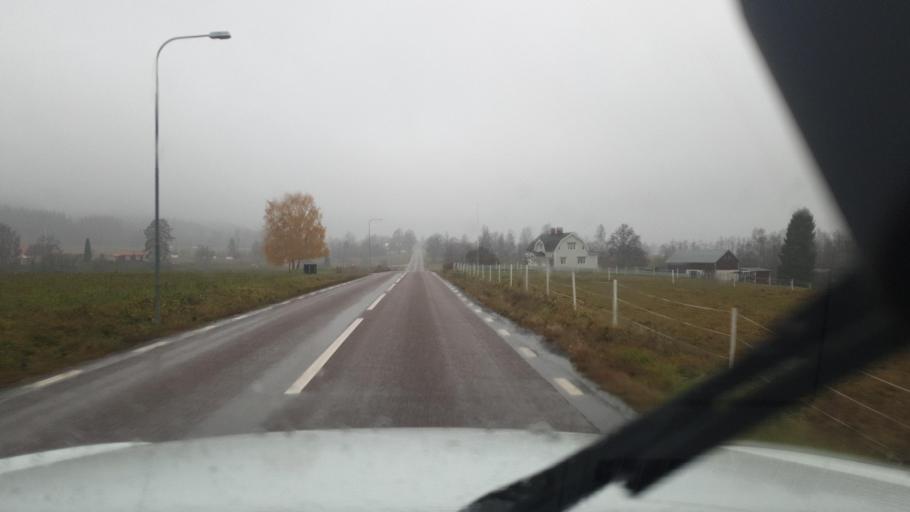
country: SE
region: Vaermland
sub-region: Sunne Kommun
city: Sunne
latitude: 59.8498
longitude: 12.9449
